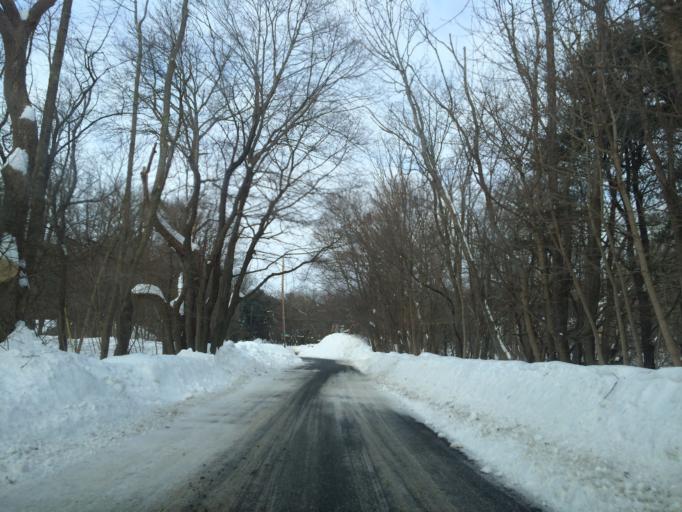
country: US
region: Massachusetts
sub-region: Middlesex County
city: Lincoln
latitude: 42.3994
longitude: -71.2988
